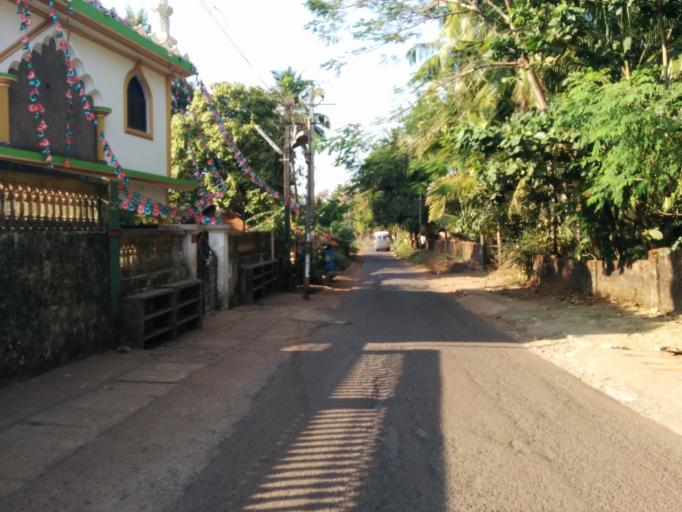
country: IN
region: Karnataka
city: Canacona
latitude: 15.0054
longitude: 74.0316
